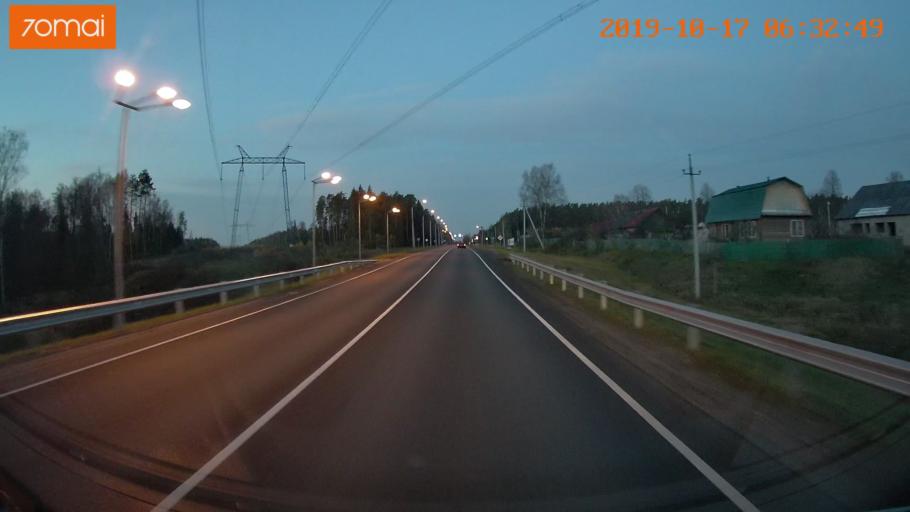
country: RU
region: Ivanovo
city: Novoye Leushino
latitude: 56.7171
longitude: 40.6699
